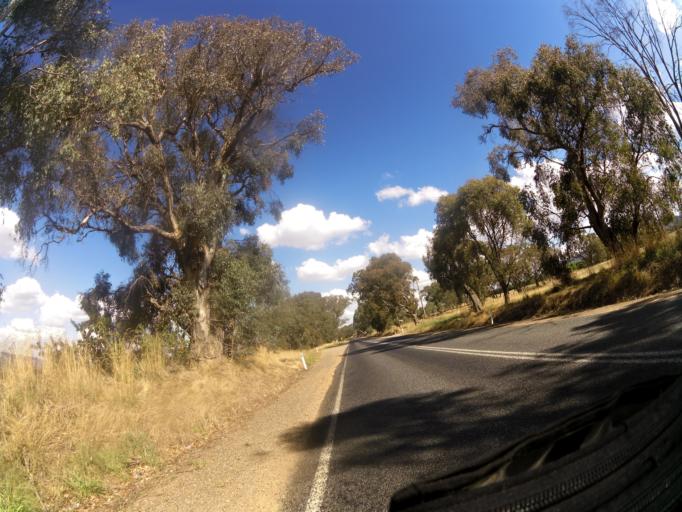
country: AU
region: Victoria
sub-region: Mansfield
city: Mansfield
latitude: -36.9146
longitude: 146.0006
